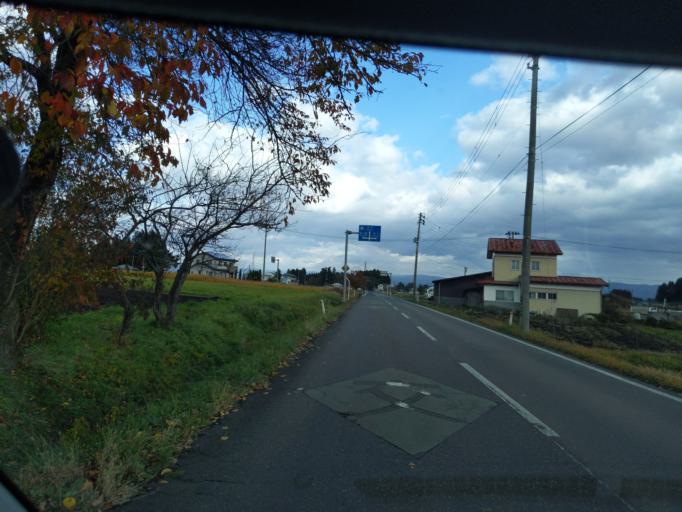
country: JP
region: Iwate
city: Mizusawa
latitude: 39.1248
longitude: 141.0735
